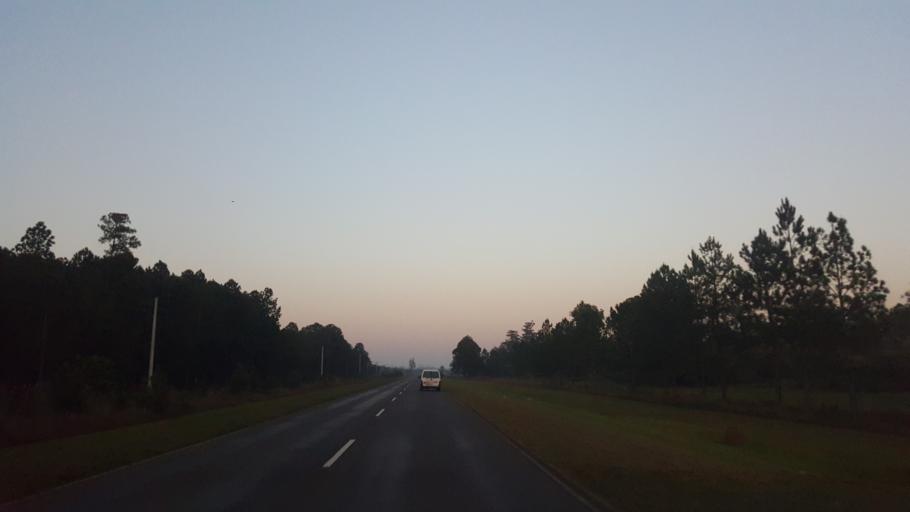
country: PY
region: Itapua
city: San Cosme y Damian
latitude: -27.6082
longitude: -56.3554
